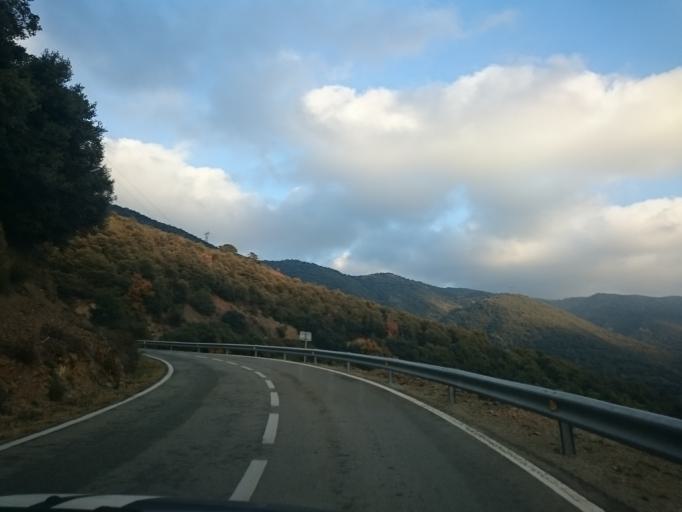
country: ES
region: Catalonia
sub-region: Provincia de Barcelona
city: Seva
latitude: 41.8166
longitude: 2.3192
